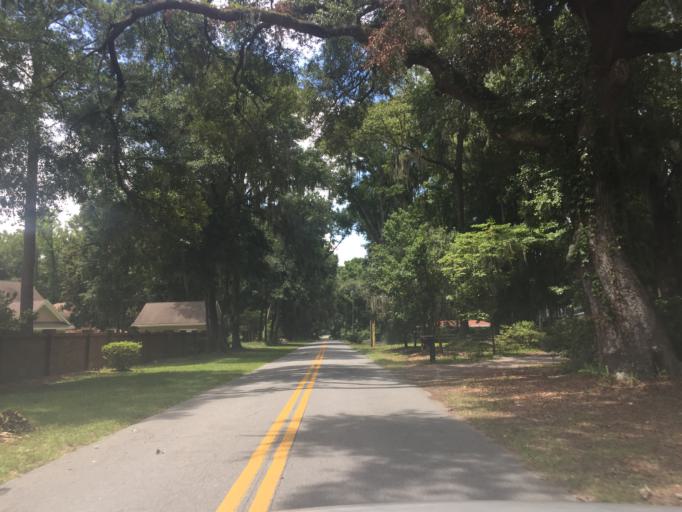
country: US
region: Georgia
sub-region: Chatham County
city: Montgomery
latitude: 31.9483
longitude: -81.1047
